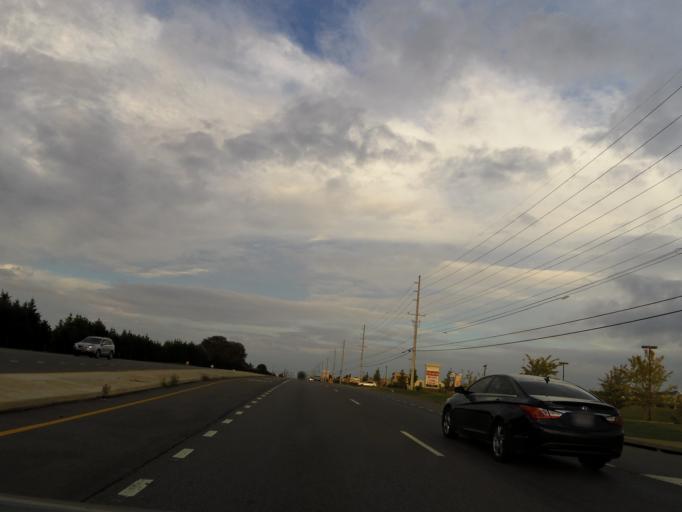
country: US
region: Alabama
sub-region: Madison County
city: Madison
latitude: 34.7502
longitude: -86.7600
